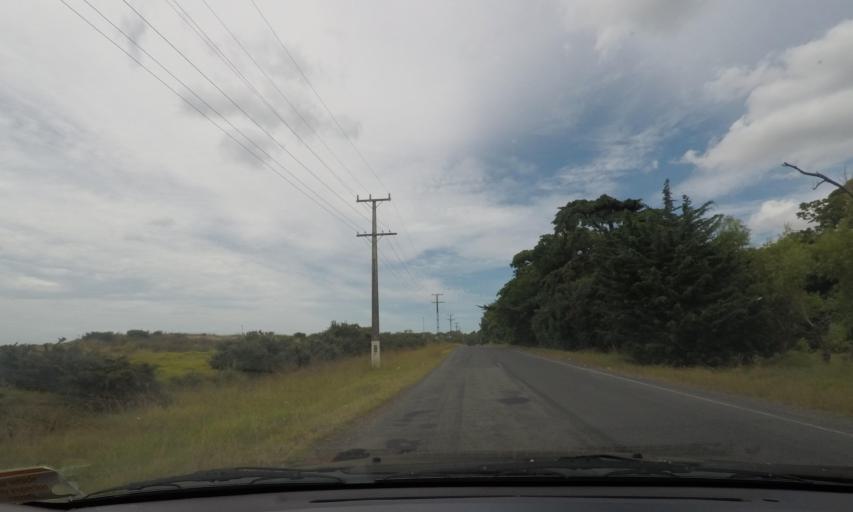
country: NZ
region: Auckland
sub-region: Auckland
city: Mangere
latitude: -36.9949
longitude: 174.7811
